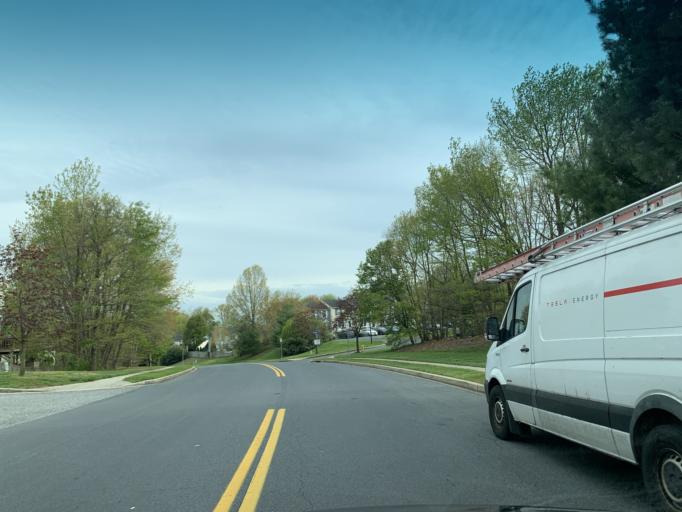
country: US
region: Maryland
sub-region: Harford County
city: Riverside
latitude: 39.4786
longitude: -76.2542
